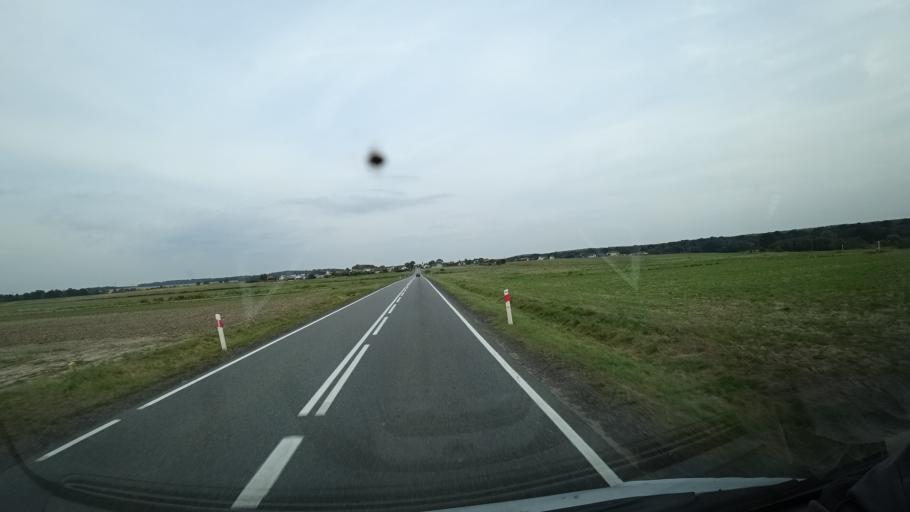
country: PL
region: Silesian Voivodeship
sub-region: Powiat gliwicki
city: Rudziniec
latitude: 50.3863
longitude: 18.4156
